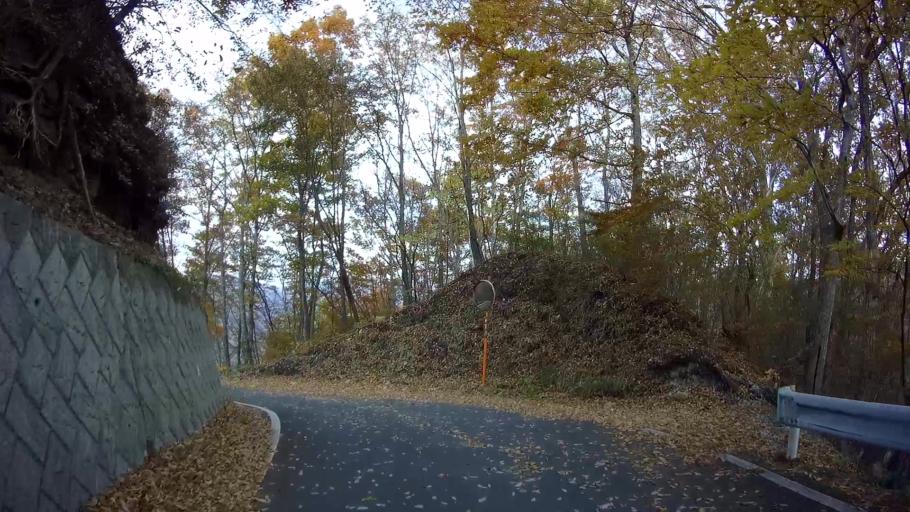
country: JP
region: Gunma
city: Nakanojomachi
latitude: 36.6332
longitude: 138.6485
